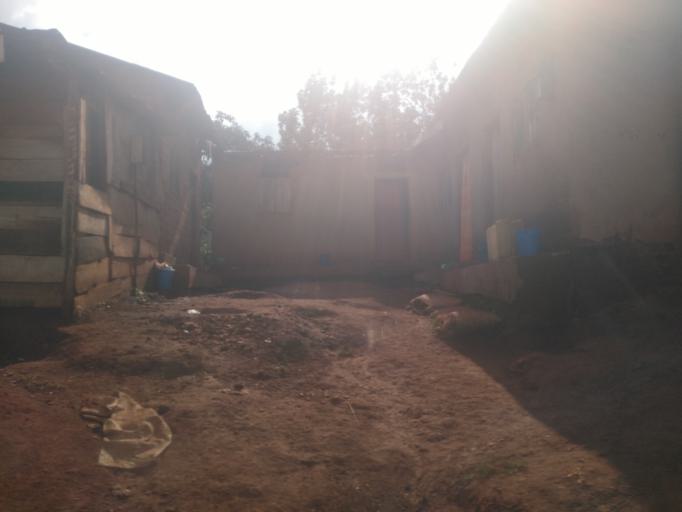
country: UG
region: Central Region
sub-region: Wakiso District
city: Kajansi
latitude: 0.2617
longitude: 32.4400
